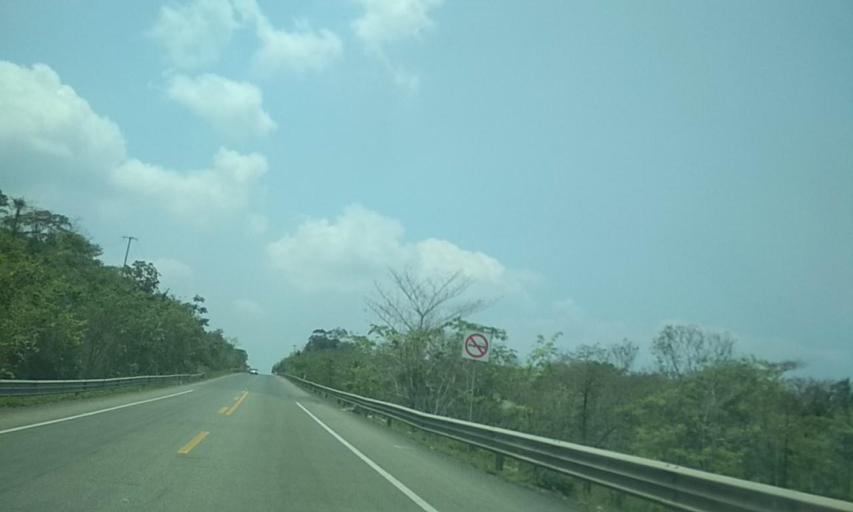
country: MX
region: Tabasco
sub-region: Huimanguillo
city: Francisco Rueda
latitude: 17.6757
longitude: -93.8778
